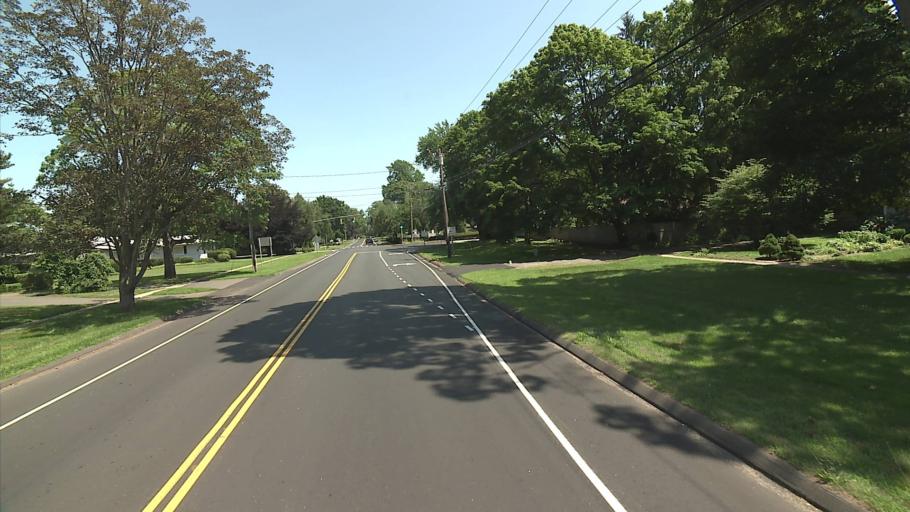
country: US
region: Connecticut
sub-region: Middlesex County
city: Old Saybrook
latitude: 41.2841
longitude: -72.3731
